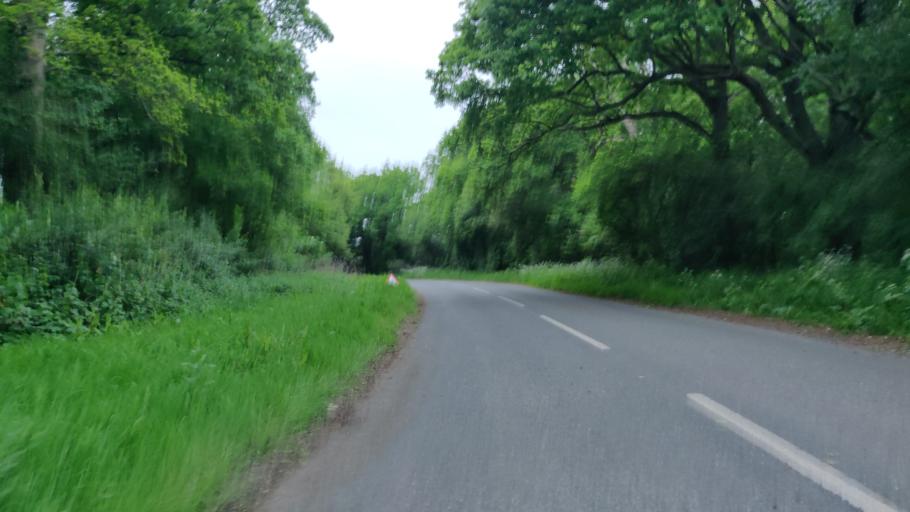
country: GB
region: England
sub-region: West Sussex
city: Partridge Green
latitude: 50.9842
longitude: -0.2998
